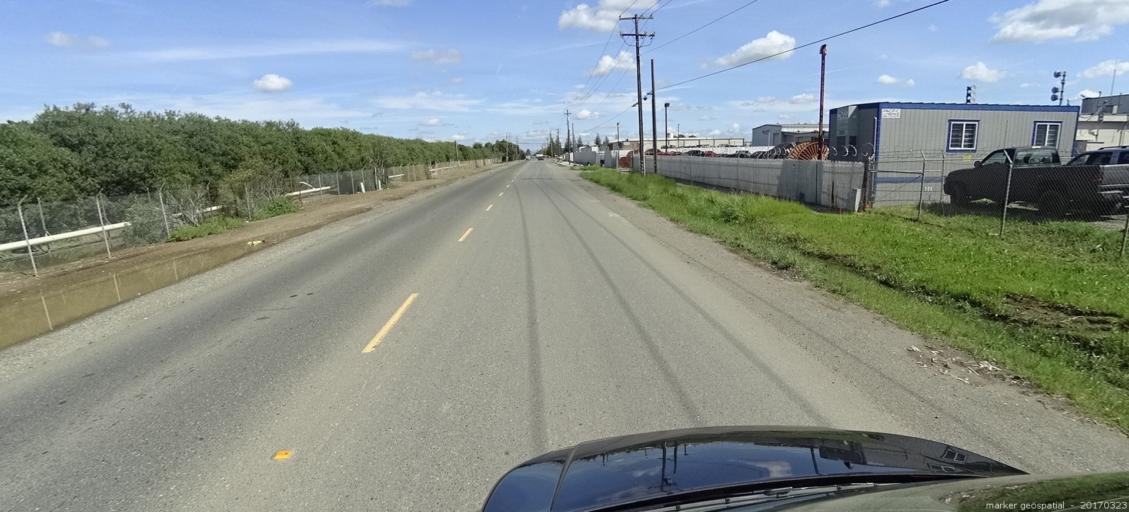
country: US
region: California
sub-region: Sacramento County
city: Rosemont
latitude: 38.5252
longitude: -121.3796
